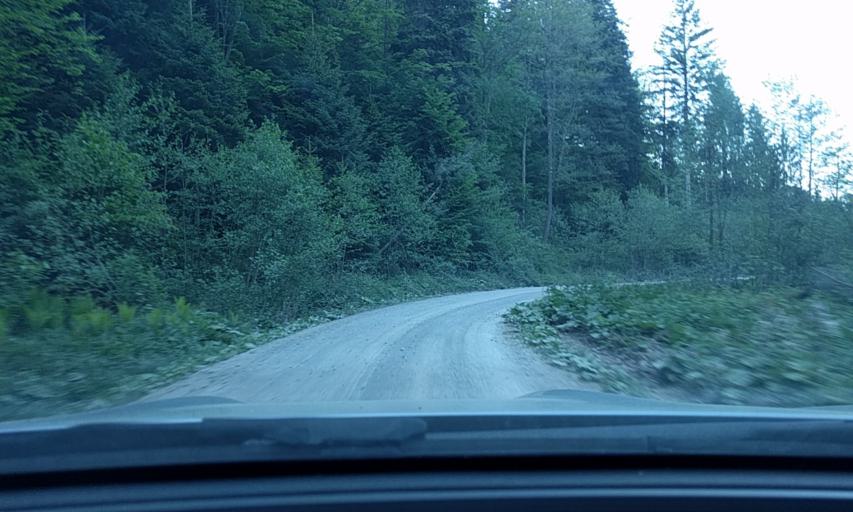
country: RO
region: Bacau
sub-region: Comuna Oituz
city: Ferestrau-Oituz
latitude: 46.1508
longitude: 26.5540
